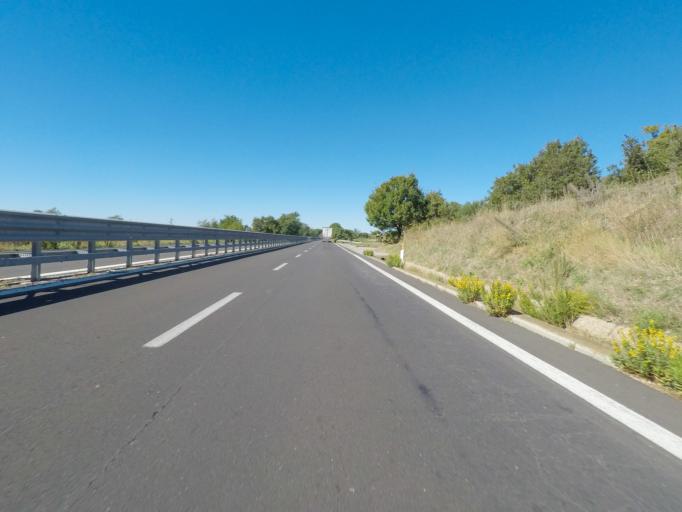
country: IT
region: Latium
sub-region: Provincia di Viterbo
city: Montalto di Castro
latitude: 42.3330
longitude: 11.6265
